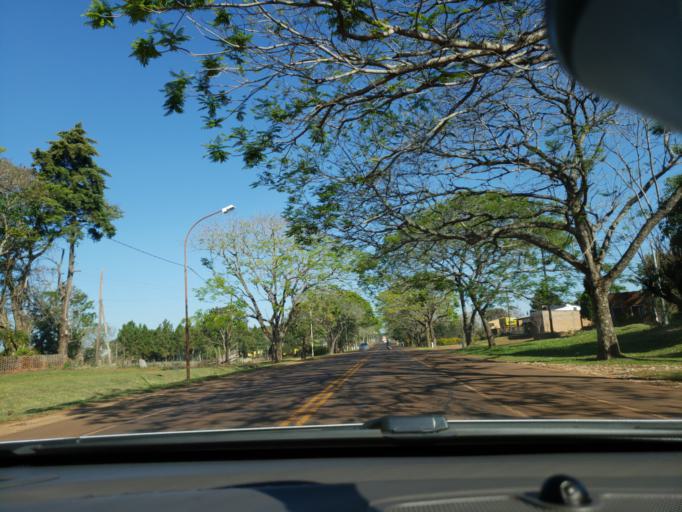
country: AR
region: Misiones
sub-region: Departamento de Apostoles
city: San Jose
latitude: -27.7684
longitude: -55.7725
